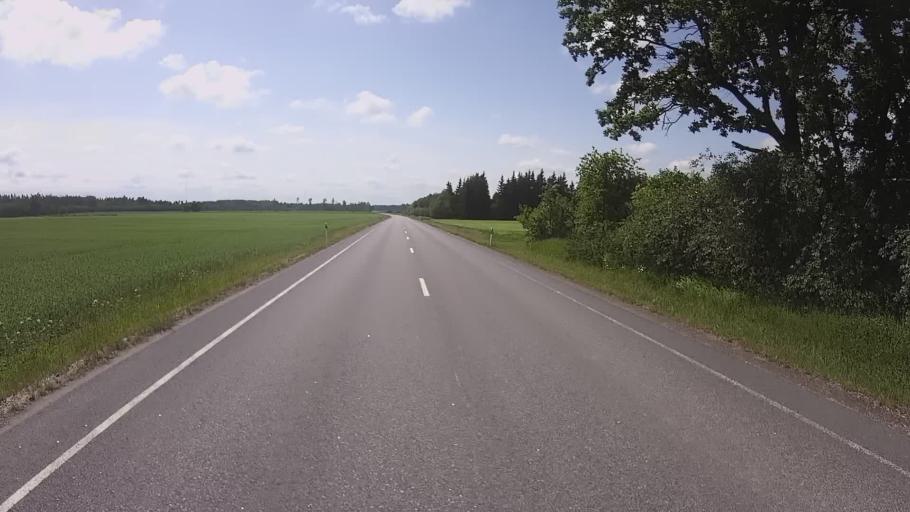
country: EE
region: Tartu
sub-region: Tartu linn
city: Tartu
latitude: 58.3935
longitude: 26.8931
